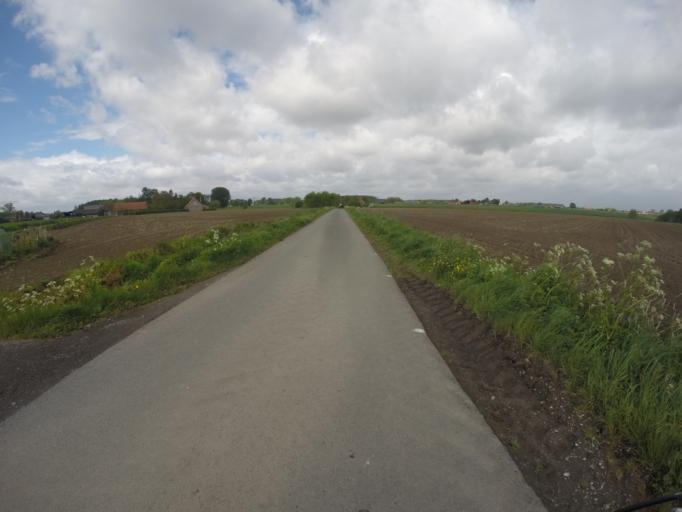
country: BE
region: Flanders
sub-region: Provincie Oost-Vlaanderen
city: Aalter
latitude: 51.0515
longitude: 3.4506
